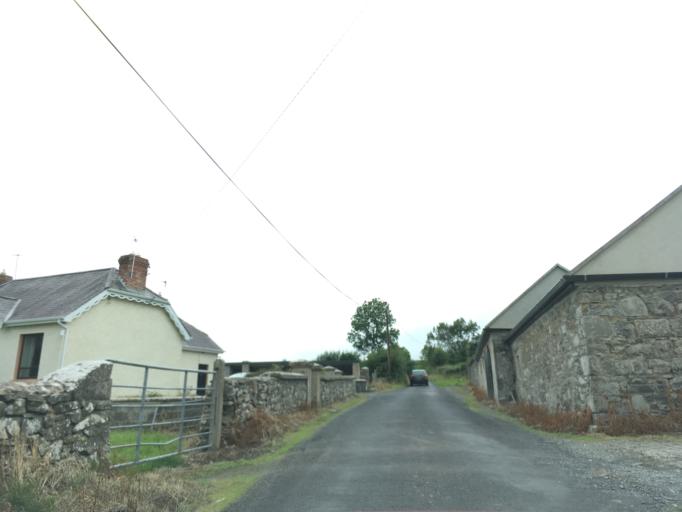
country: IE
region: Munster
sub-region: An Clar
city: Ennis
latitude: 52.7287
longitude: -9.0670
